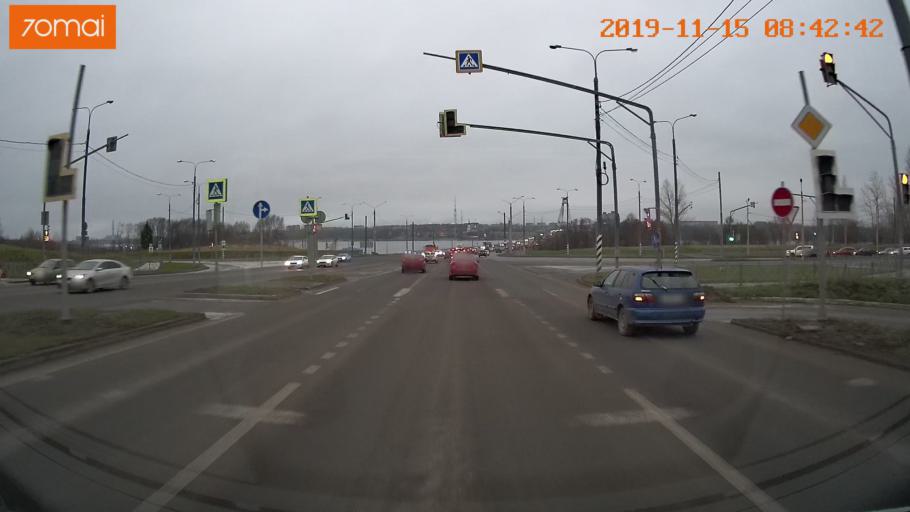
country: RU
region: Vologda
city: Cherepovets
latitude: 59.1047
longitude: 37.9068
